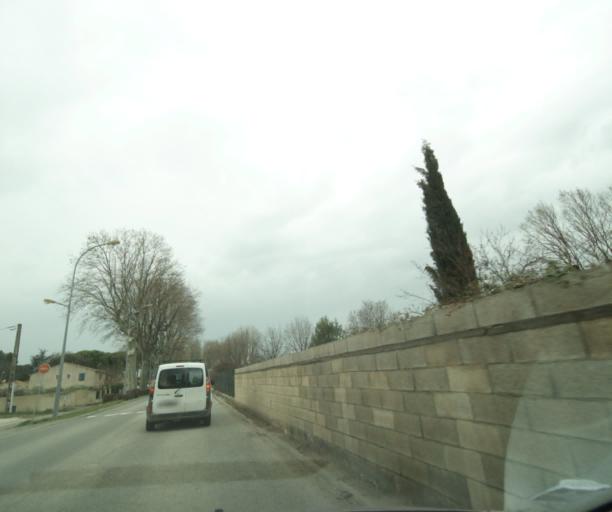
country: FR
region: Provence-Alpes-Cote d'Azur
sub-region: Departement des Bouches-du-Rhone
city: Peyrolles-en-Provence
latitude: 43.6460
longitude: 5.5919
